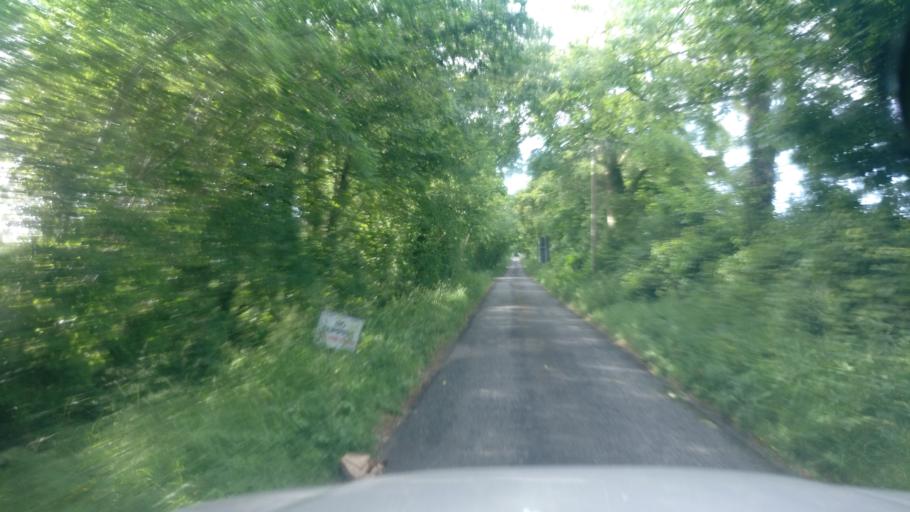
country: IE
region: Connaught
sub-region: County Galway
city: Ballinasloe
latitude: 53.2284
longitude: -8.2279
